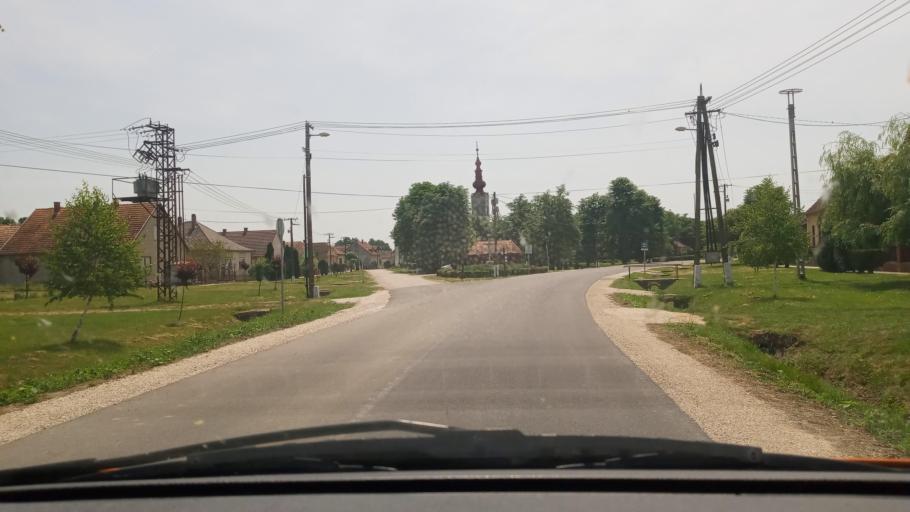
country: HU
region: Baranya
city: Szigetvar
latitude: 45.9623
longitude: 17.6586
